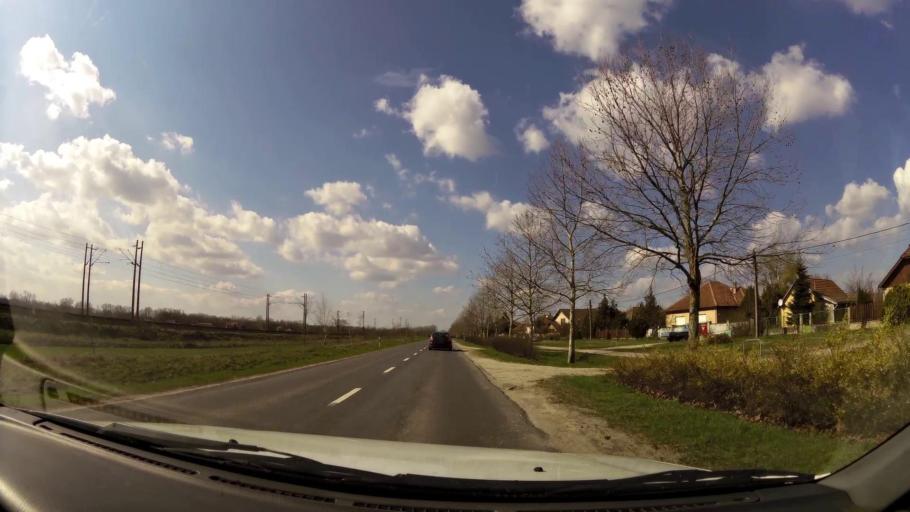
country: HU
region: Pest
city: Nagykata
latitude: 47.3989
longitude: 19.7574
